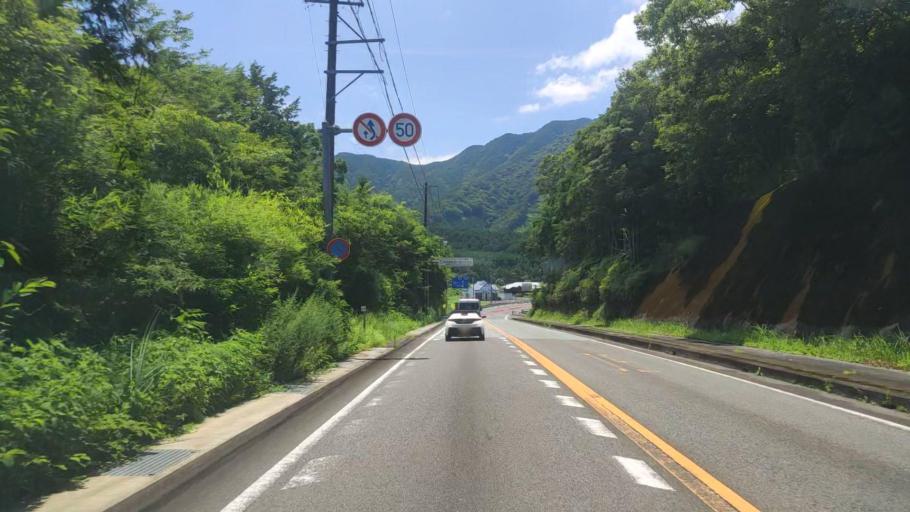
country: JP
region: Mie
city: Owase
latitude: 34.1416
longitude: 136.2423
